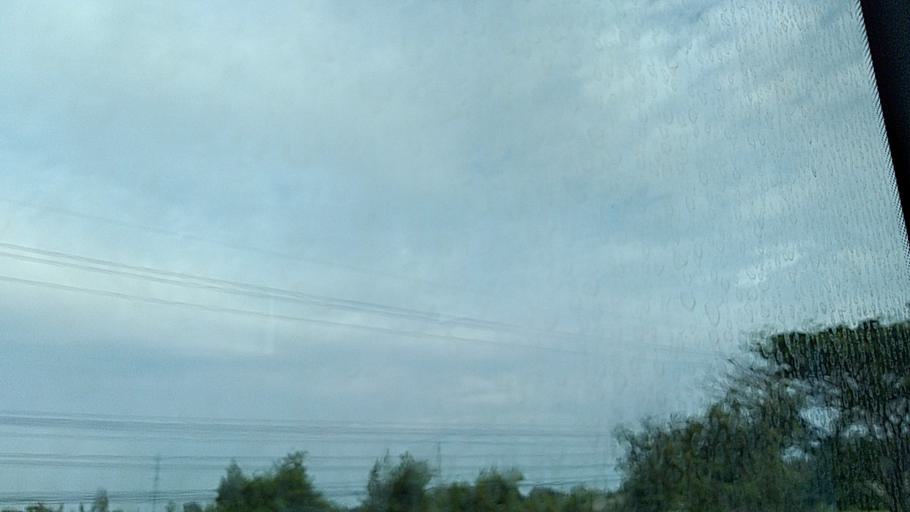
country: TH
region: Roi Et
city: Changhan
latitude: 16.0938
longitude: 103.5419
